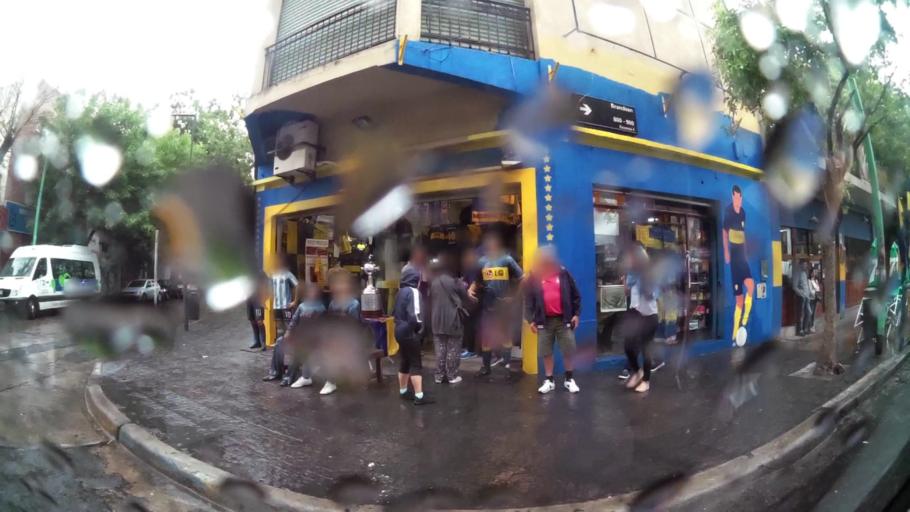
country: AR
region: Buenos Aires
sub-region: Partido de Avellaneda
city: Avellaneda
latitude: -34.6368
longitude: -58.3648
